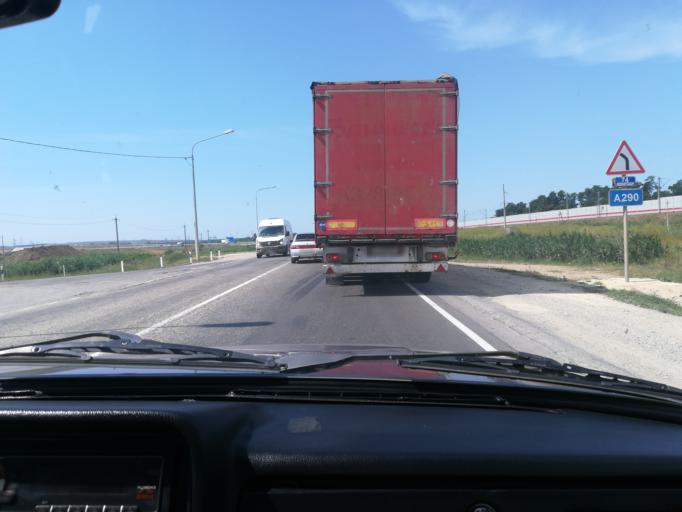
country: RU
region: Krasnodarskiy
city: Dzhiginka
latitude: 45.1306
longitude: 37.3240
